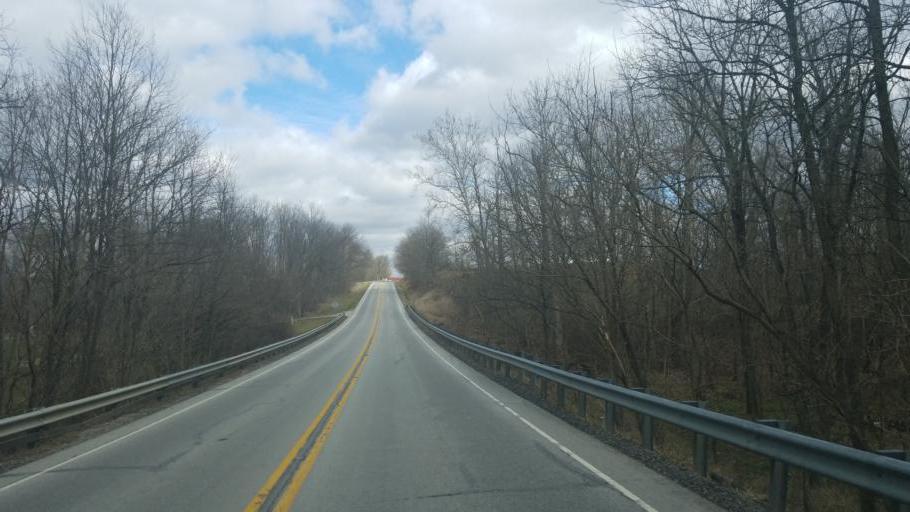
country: US
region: Indiana
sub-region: Parke County
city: Rockville
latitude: 39.7579
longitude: -87.1304
